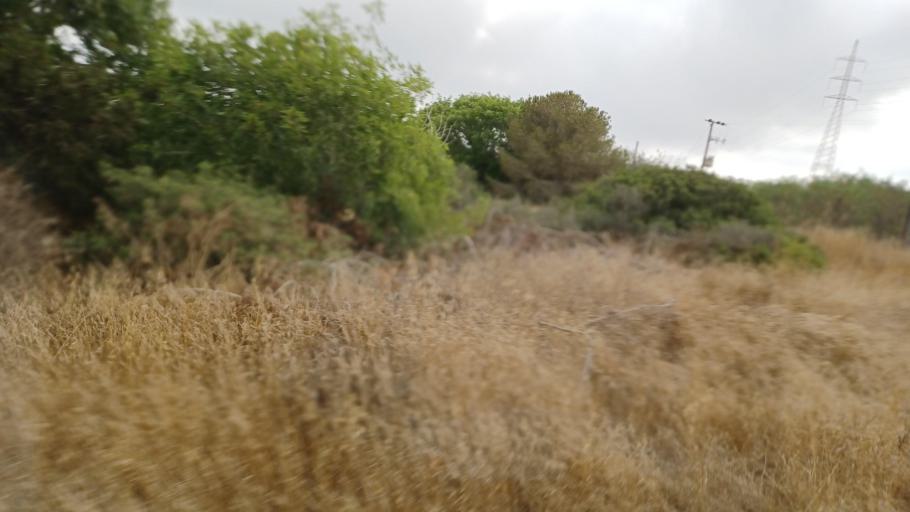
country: CY
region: Ammochostos
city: Protaras
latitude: 35.0115
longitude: 34.0230
